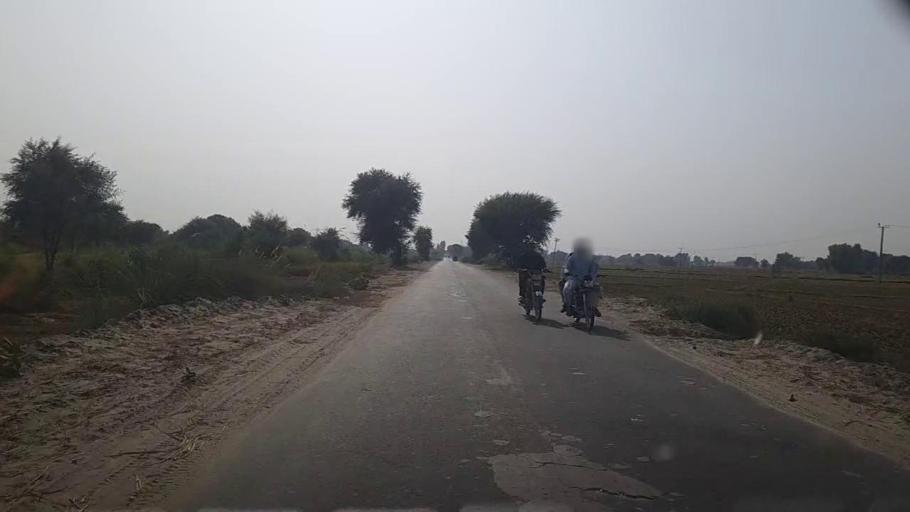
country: PK
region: Sindh
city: Kashmor
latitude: 28.3998
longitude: 69.5491
